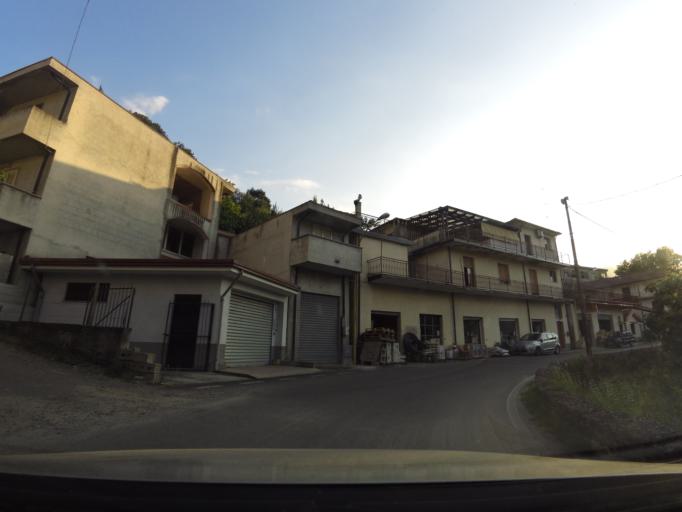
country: IT
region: Calabria
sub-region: Provincia di Reggio Calabria
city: Bivongi
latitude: 38.4815
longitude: 16.4542
